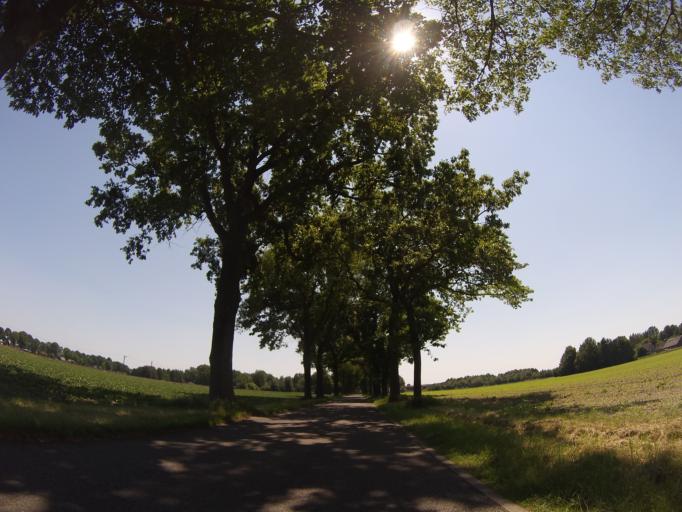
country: NL
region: Drenthe
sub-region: Gemeente Coevorden
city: Sleen
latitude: 52.7291
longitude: 6.8518
